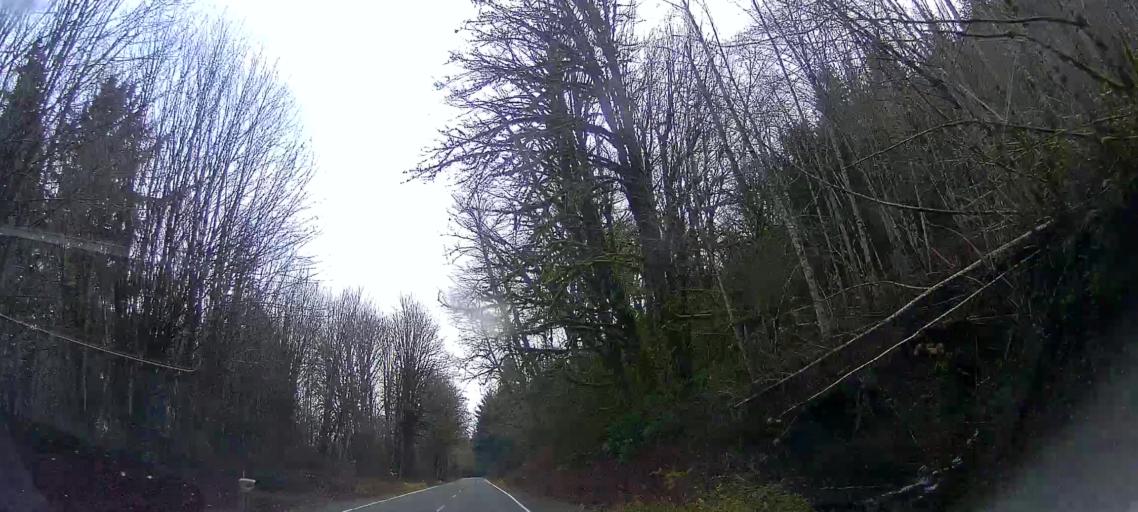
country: US
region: Washington
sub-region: Skagit County
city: Sedro-Woolley
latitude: 48.5128
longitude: -121.9367
